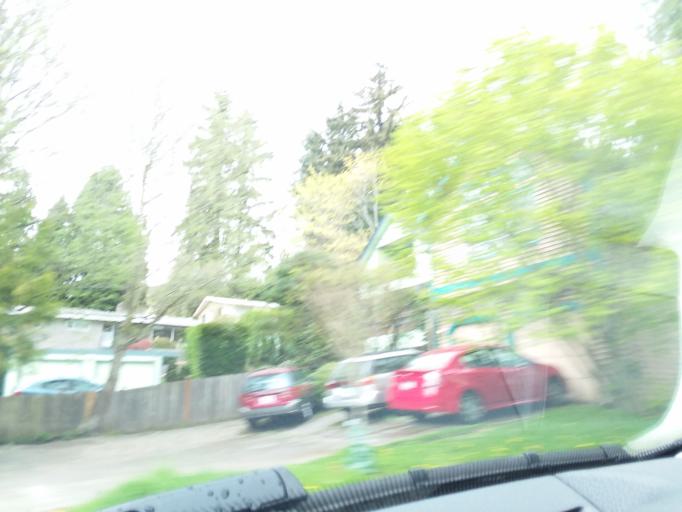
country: US
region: Washington
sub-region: King County
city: Lake Forest Park
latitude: 47.6936
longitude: -122.3031
